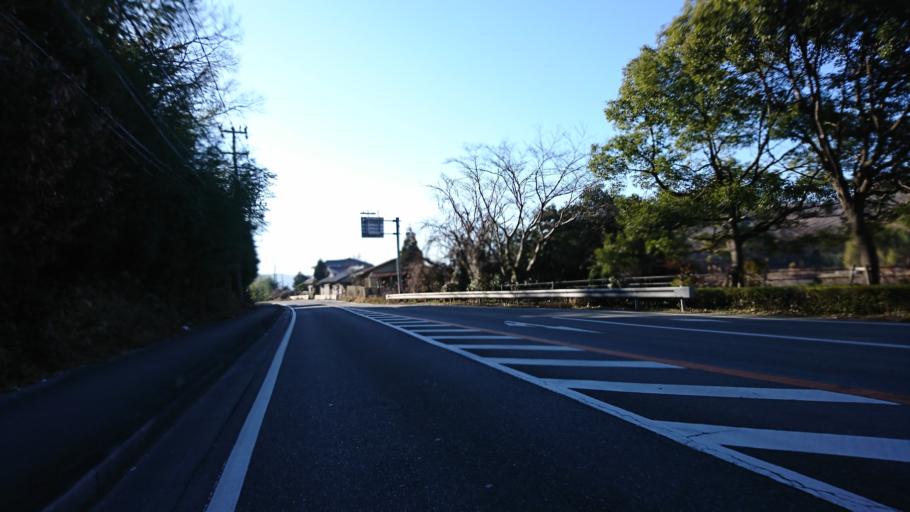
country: JP
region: Hyogo
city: Kakogawacho-honmachi
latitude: 34.8452
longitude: 134.8361
